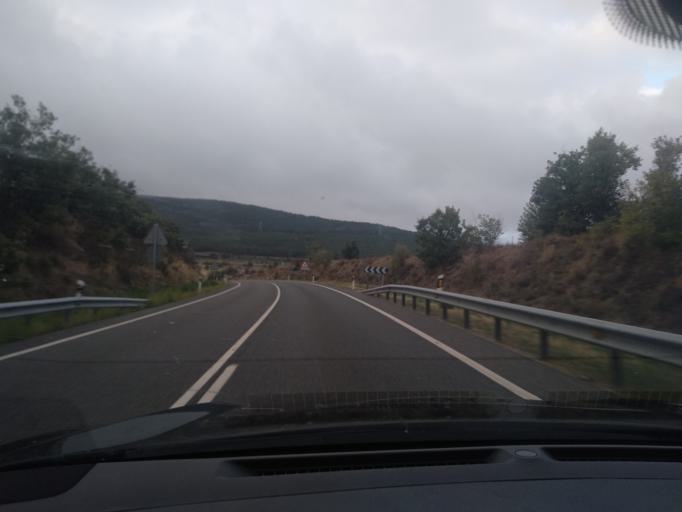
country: ES
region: Castille and Leon
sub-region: Provincia de Segovia
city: Otero de Herreros
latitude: 40.7413
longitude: -4.2028
